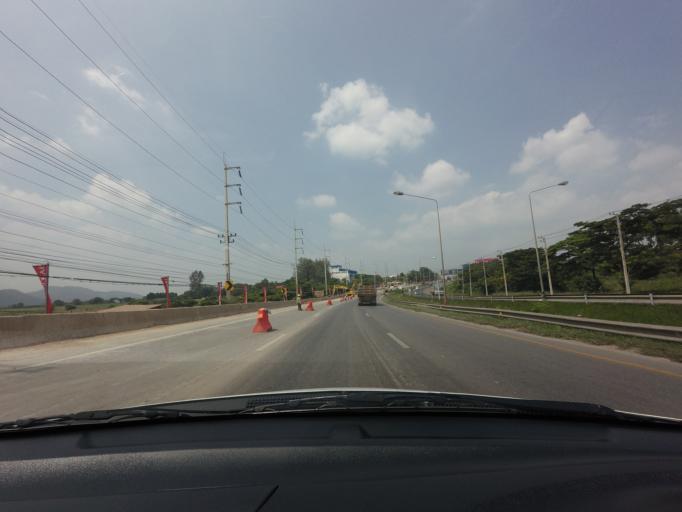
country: TH
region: Nakhon Ratchasima
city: Pak Chong
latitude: 14.6524
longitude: 101.3519
